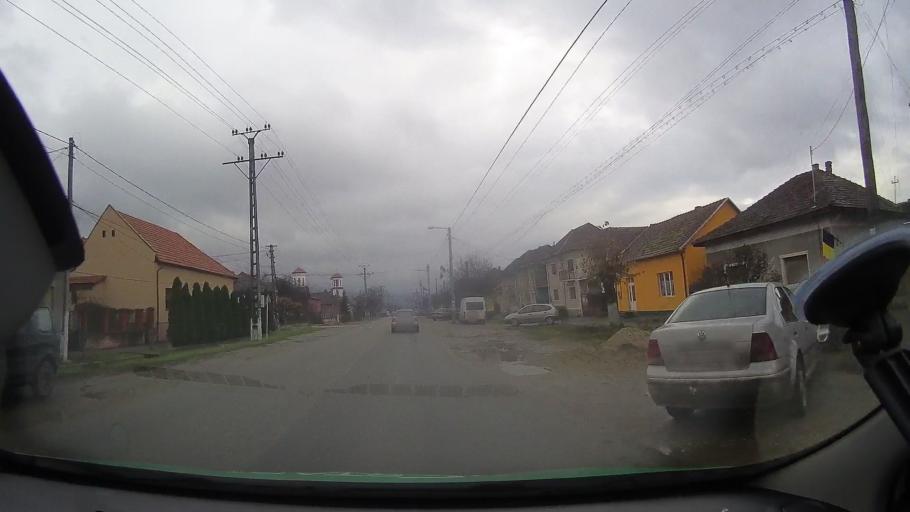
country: RO
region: Arad
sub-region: Comuna Sebis
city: Sebis
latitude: 46.3692
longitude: 22.1310
